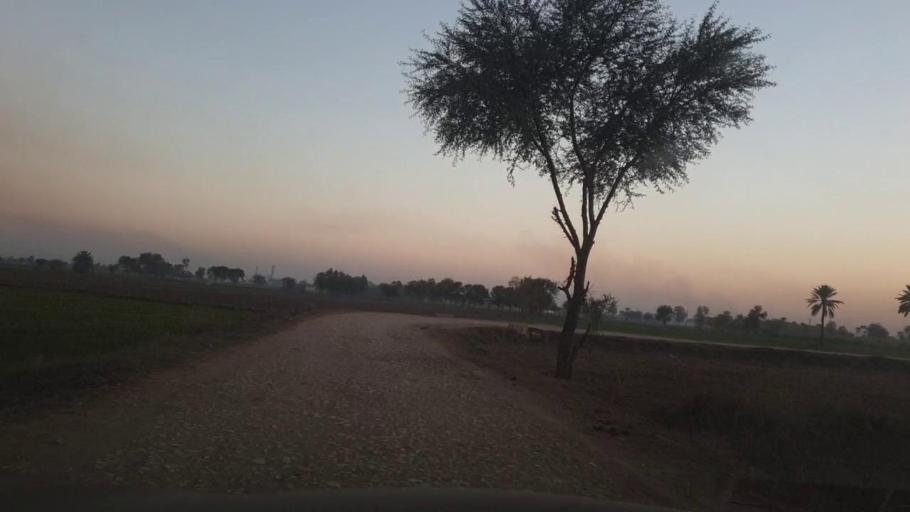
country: PK
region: Sindh
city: Ghotki
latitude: 28.0428
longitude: 69.3552
